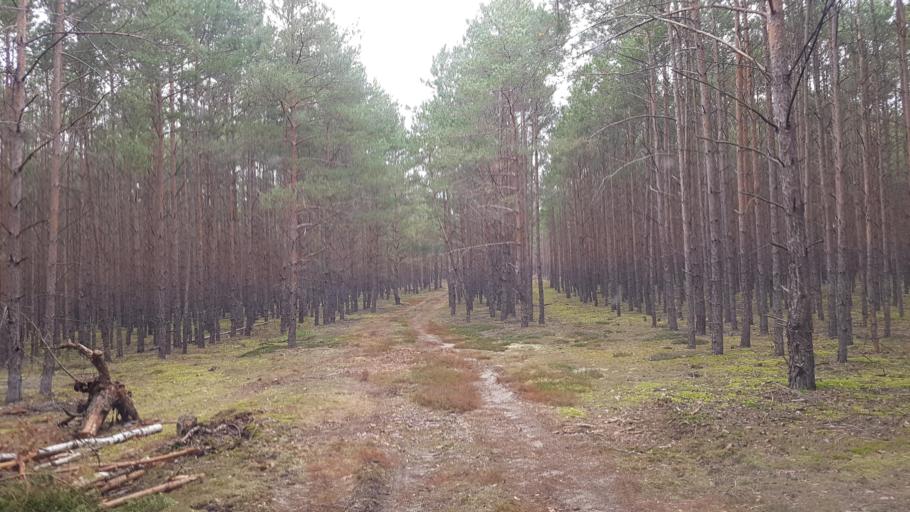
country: DE
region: Brandenburg
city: Doberlug-Kirchhain
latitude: 51.6110
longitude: 13.6216
